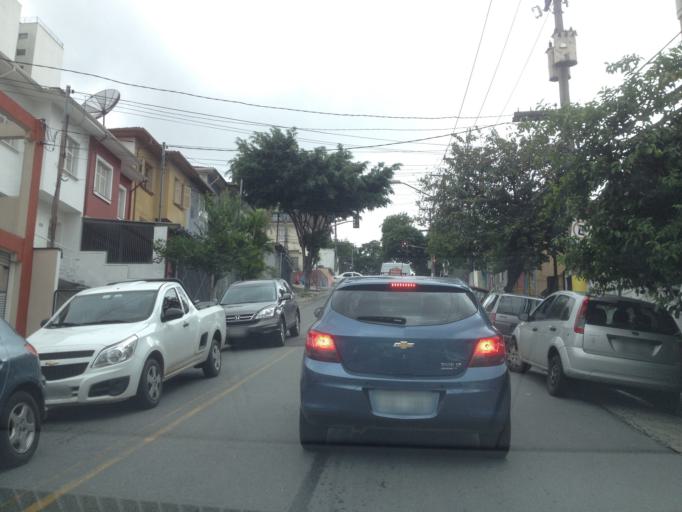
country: BR
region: Sao Paulo
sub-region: Sao Paulo
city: Sao Paulo
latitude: -23.5550
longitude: -46.6930
